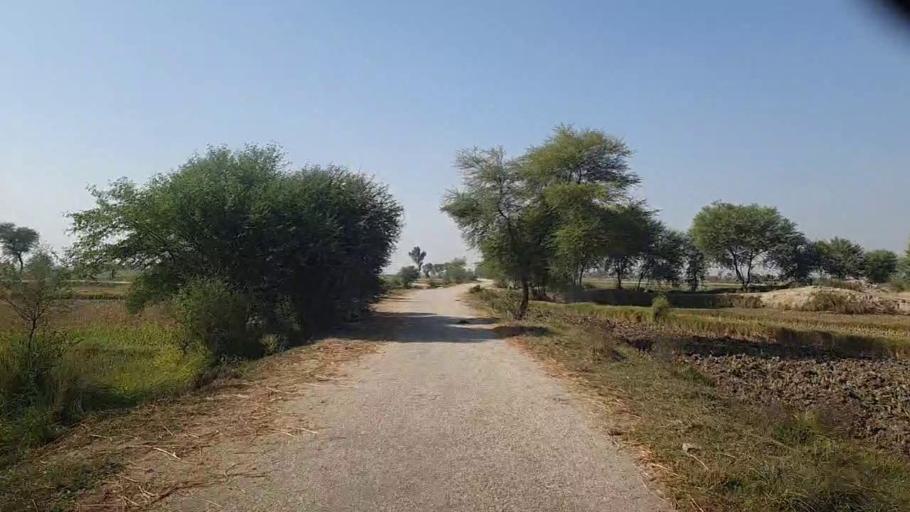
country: PK
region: Sindh
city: Tangwani
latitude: 28.2455
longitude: 68.9493
